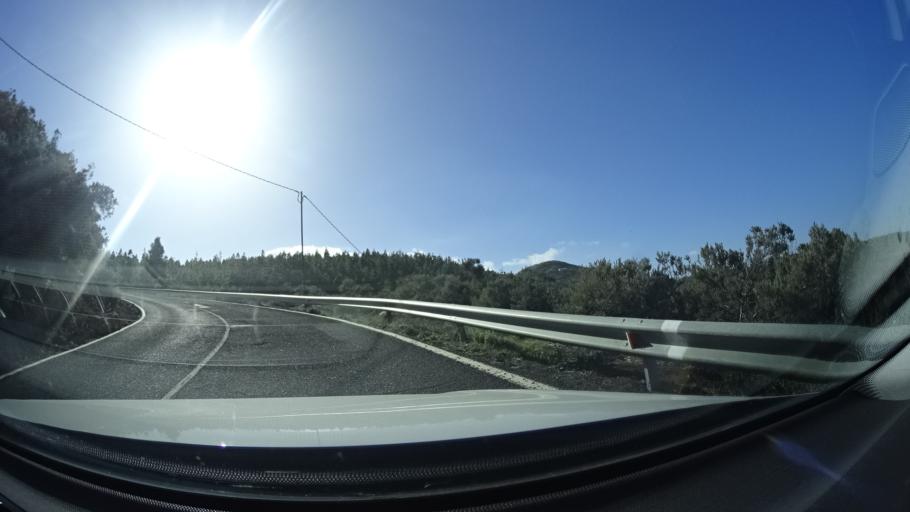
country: ES
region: Canary Islands
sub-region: Provincia de Las Palmas
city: San Bartolome
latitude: 27.9648
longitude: -15.5500
